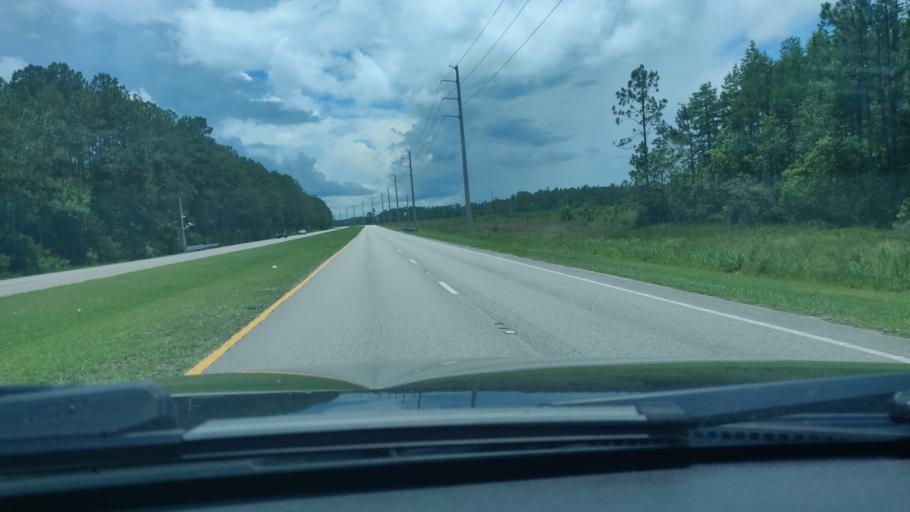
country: US
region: Florida
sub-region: Flagler County
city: Bunnell
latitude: 29.5190
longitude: -81.2629
